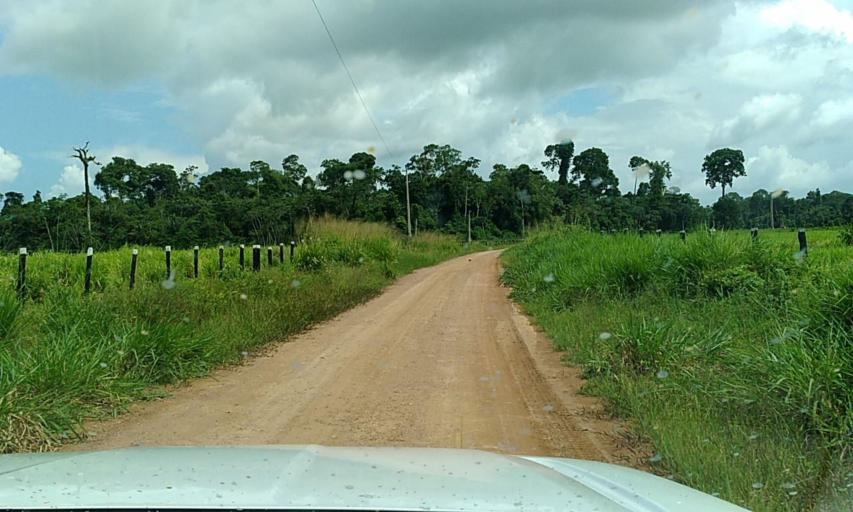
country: BR
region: Para
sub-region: Senador Jose Porfirio
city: Senador Jose Porfirio
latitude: -2.5150
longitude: -51.8401
